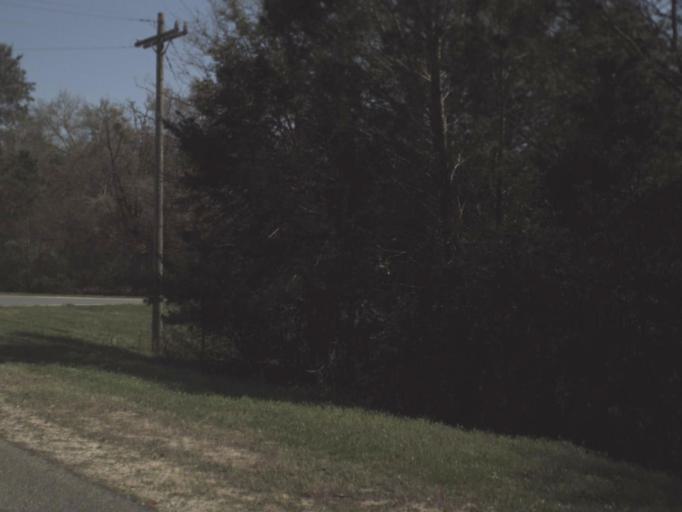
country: US
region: Florida
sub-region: Liberty County
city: Bristol
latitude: 30.4242
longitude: -84.9208
